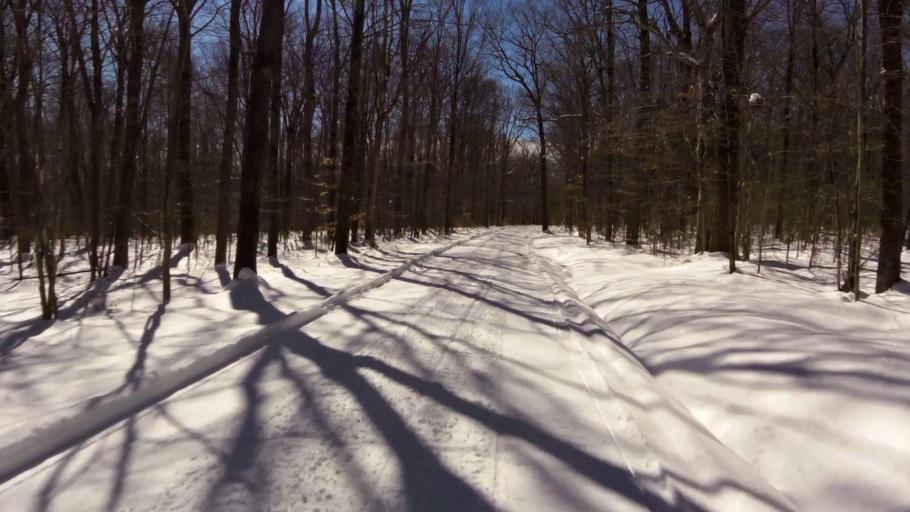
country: US
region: New York
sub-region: Allegany County
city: Houghton
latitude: 42.3520
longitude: -78.1944
